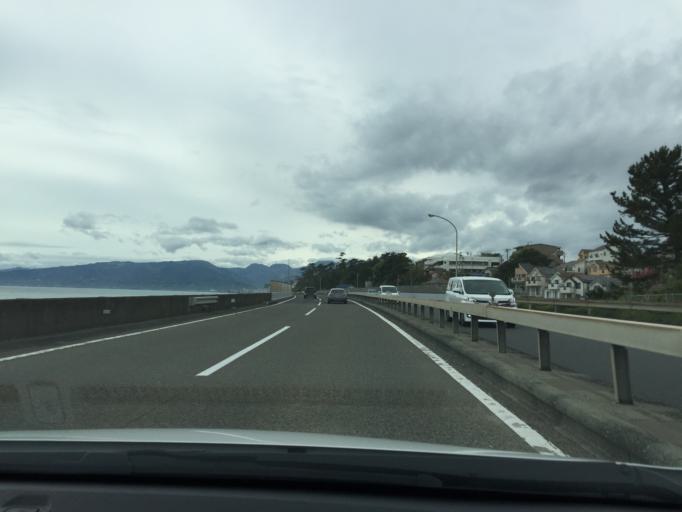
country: JP
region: Kanagawa
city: Ninomiya
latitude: 35.2934
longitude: 139.2505
